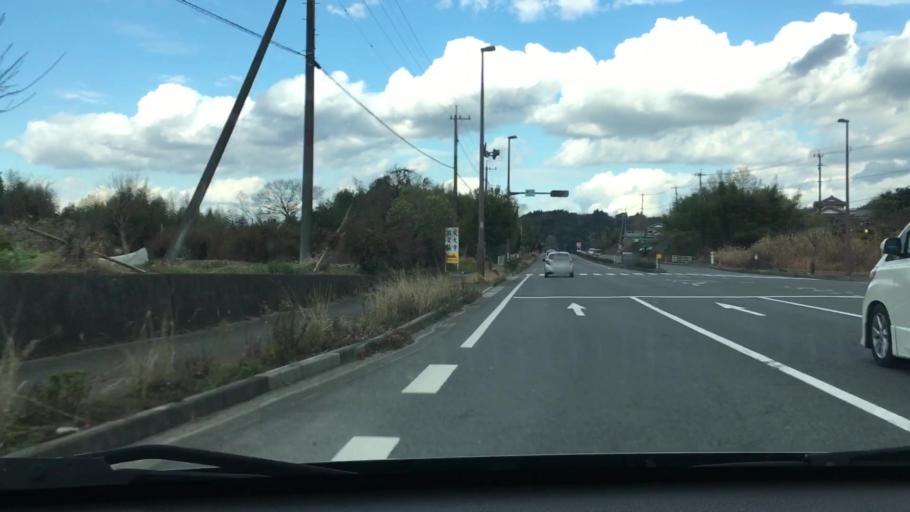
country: JP
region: Oita
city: Oita
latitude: 33.1267
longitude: 131.6561
